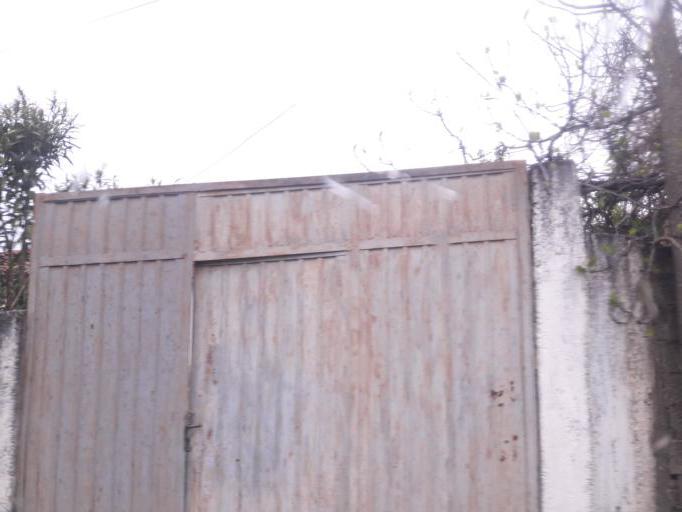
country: AL
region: Shkoder
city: Vukatane
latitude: 42.0090
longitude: 19.5353
